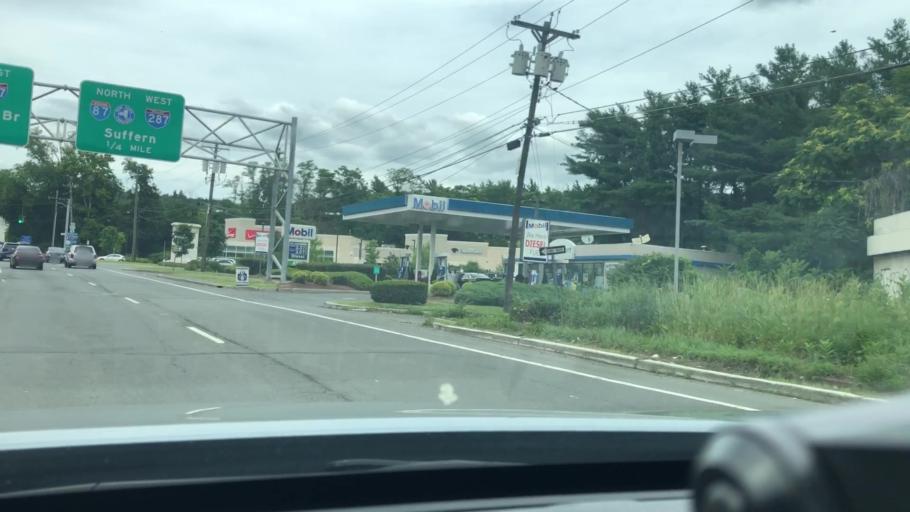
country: US
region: New York
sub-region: Rockland County
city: Valley Cottage
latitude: 41.0976
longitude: -73.9504
